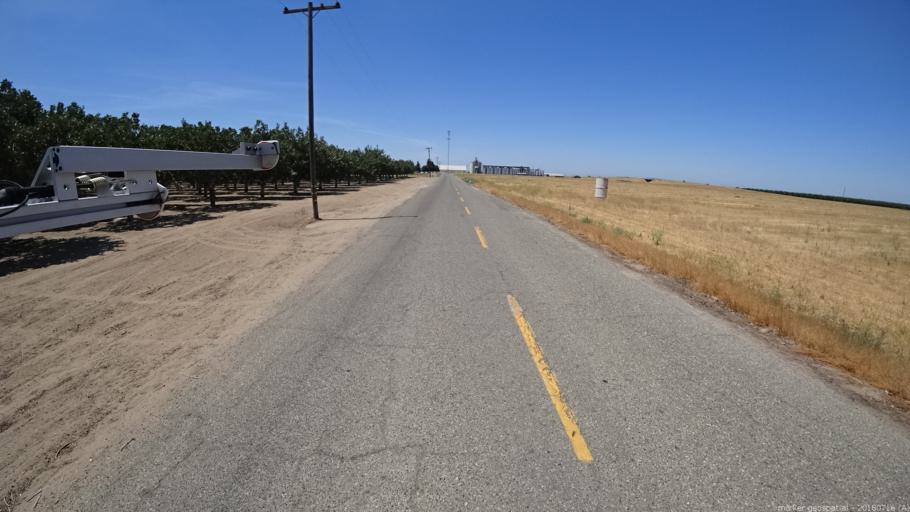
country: US
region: California
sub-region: Madera County
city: Fairmead
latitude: 37.0456
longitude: -120.1484
